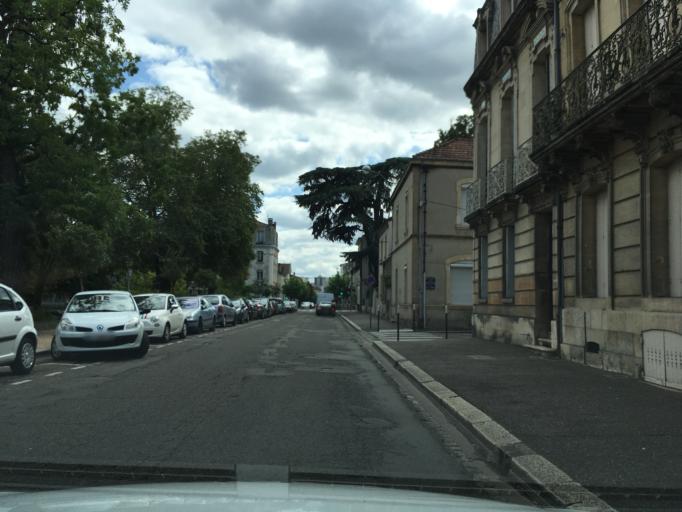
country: FR
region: Aquitaine
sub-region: Departement du Lot-et-Garonne
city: Agen
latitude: 44.2003
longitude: 0.6204
